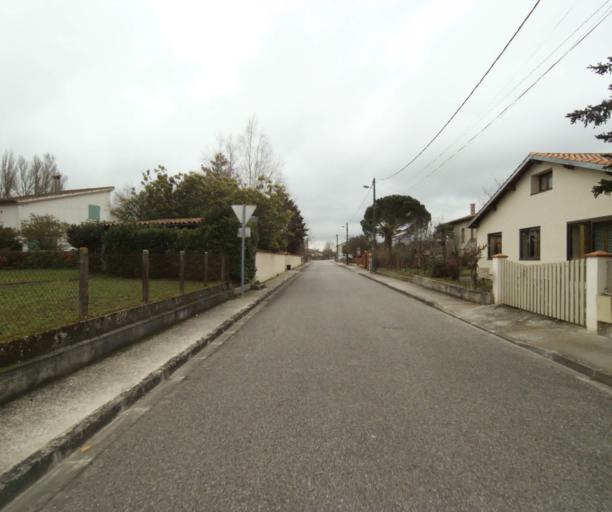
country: FR
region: Midi-Pyrenees
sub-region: Departement de l'Ariege
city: Mazeres
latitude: 43.2486
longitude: 1.6811
